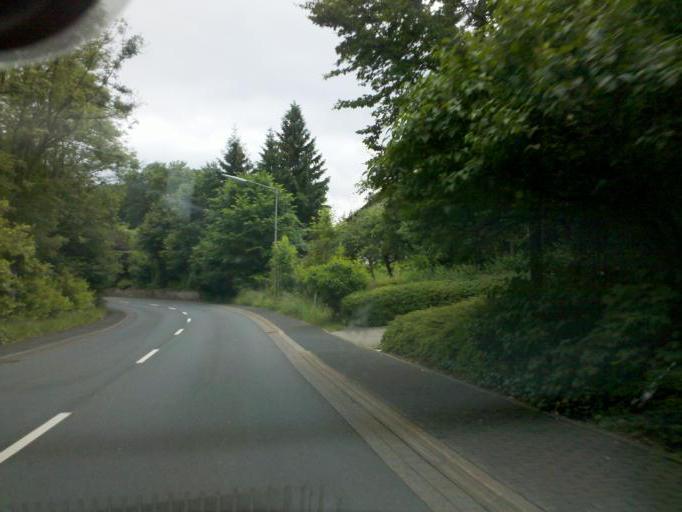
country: DE
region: North Rhine-Westphalia
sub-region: Regierungsbezirk Arnsberg
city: Wilnsdorf
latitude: 50.8434
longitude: 8.0725
